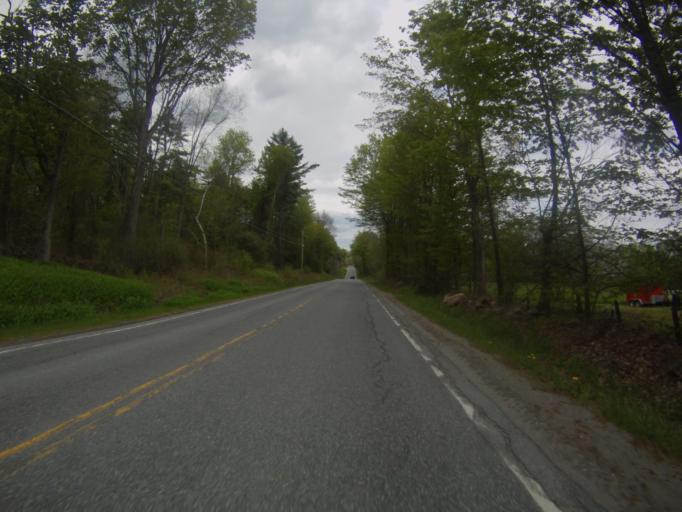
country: US
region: New York
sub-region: Essex County
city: Port Henry
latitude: 44.0274
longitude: -73.5013
